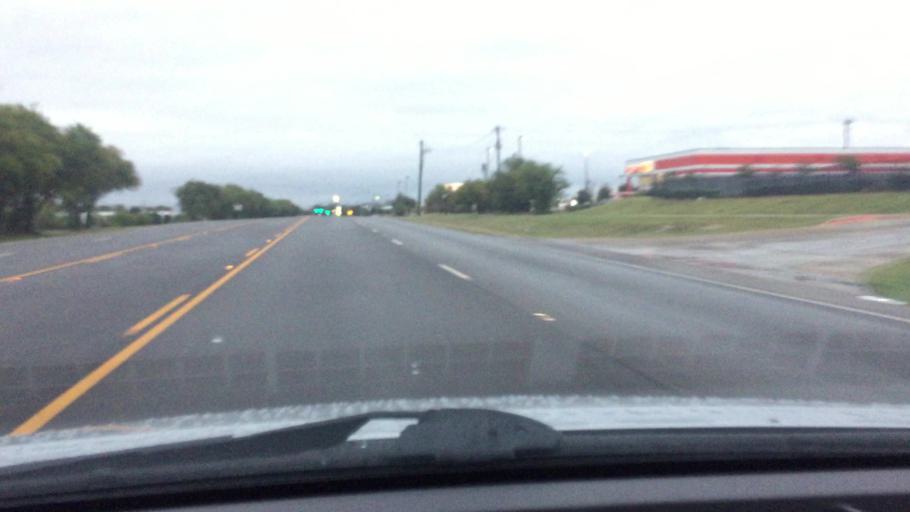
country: US
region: Texas
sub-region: Williamson County
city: Leander
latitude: 30.5645
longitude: -97.8470
